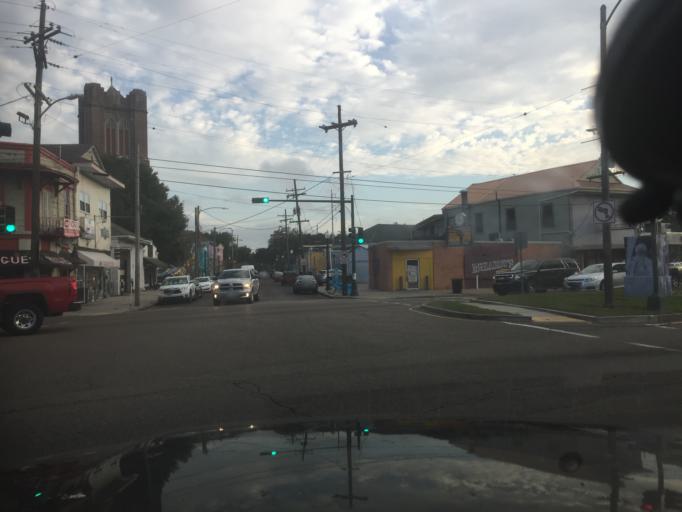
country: US
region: Louisiana
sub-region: Orleans Parish
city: New Orleans
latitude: 29.9775
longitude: -90.0771
